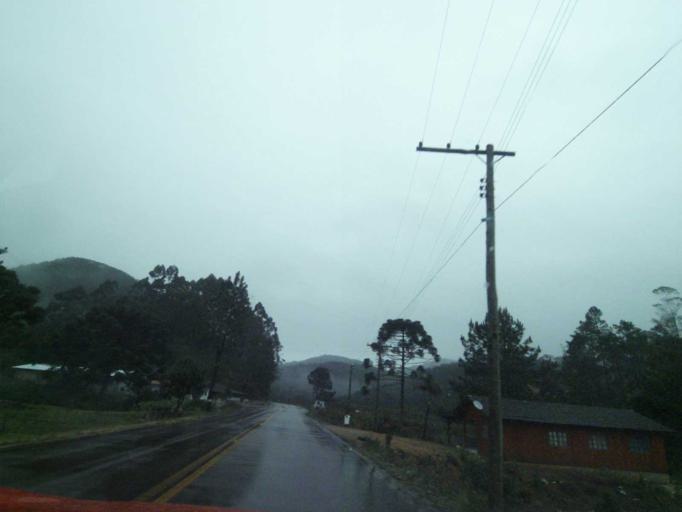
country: BR
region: Santa Catarina
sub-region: Anitapolis
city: Anitapolis
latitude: -27.8431
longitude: -49.0517
